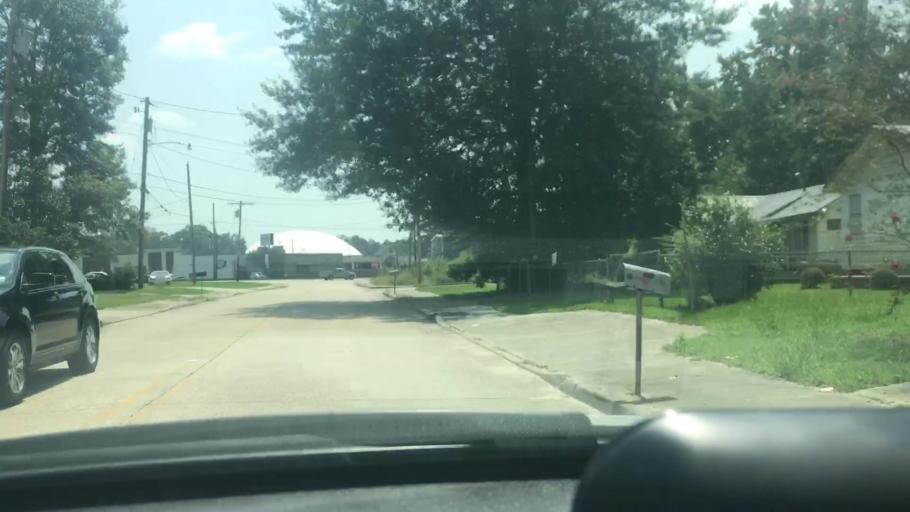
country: US
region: Louisiana
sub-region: Livingston Parish
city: Denham Springs
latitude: 30.4760
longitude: -90.9577
